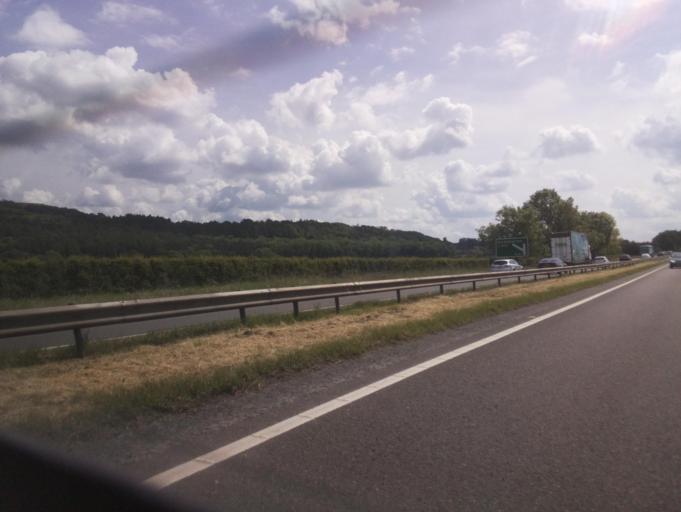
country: GB
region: England
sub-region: North Yorkshire
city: Northallerton
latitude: 54.3789
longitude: -1.3209
